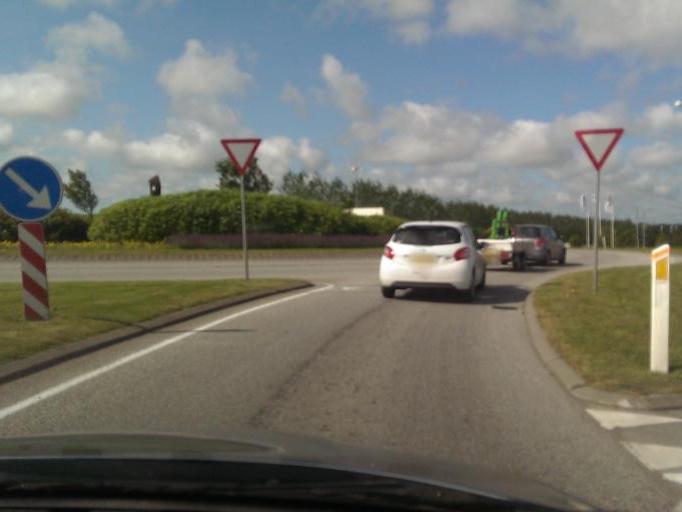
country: DK
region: North Denmark
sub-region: Bronderslev Kommune
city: Bronderslev
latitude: 57.2526
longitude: 9.9675
